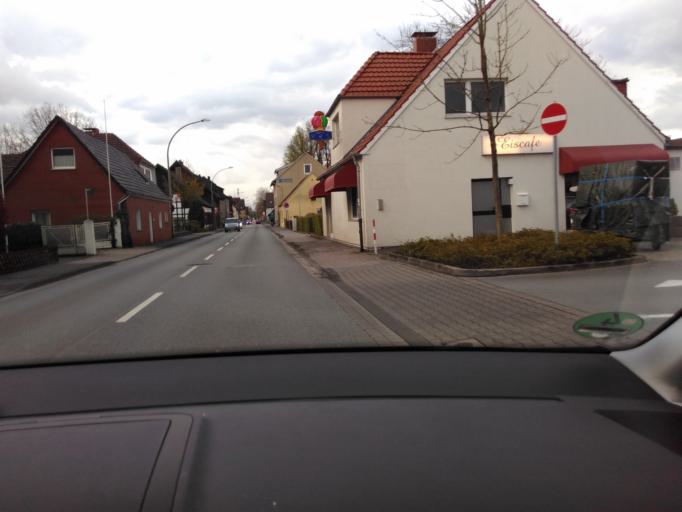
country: DE
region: North Rhine-Westphalia
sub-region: Regierungsbezirk Detmold
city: Verl
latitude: 51.9390
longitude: 8.4865
